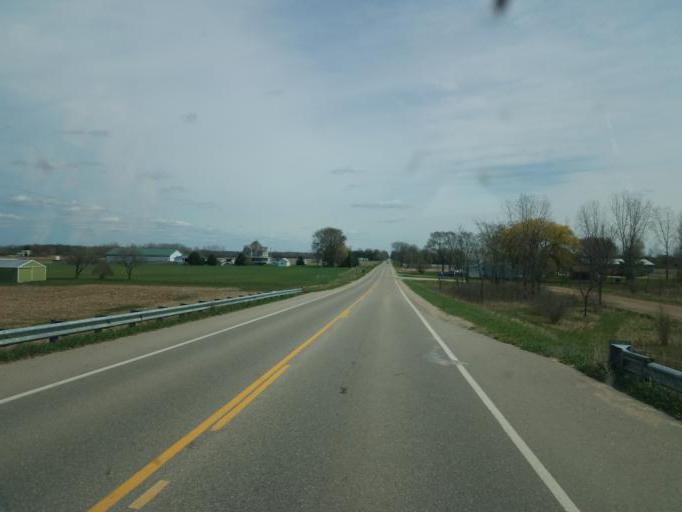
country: US
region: Michigan
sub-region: Isabella County
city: Mount Pleasant
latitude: 43.6406
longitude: -84.7569
